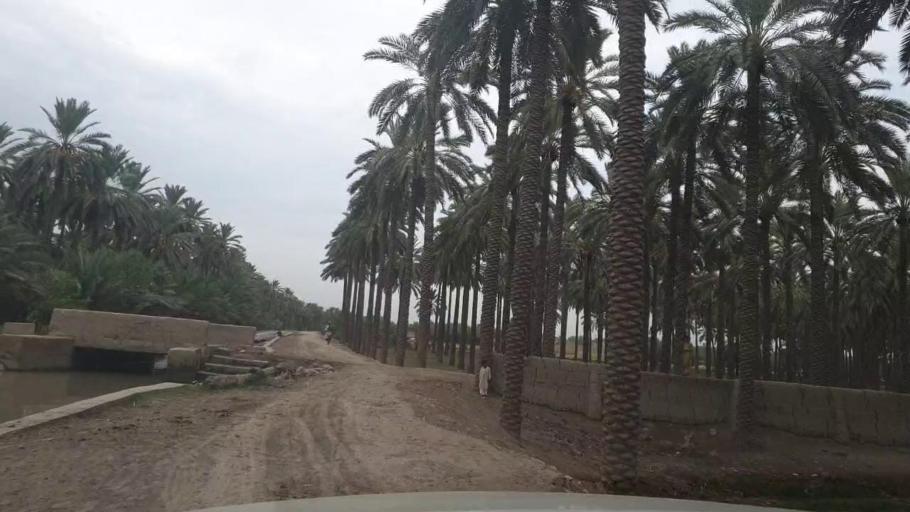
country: PK
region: Sindh
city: Sukkur
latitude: 27.6284
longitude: 68.8203
